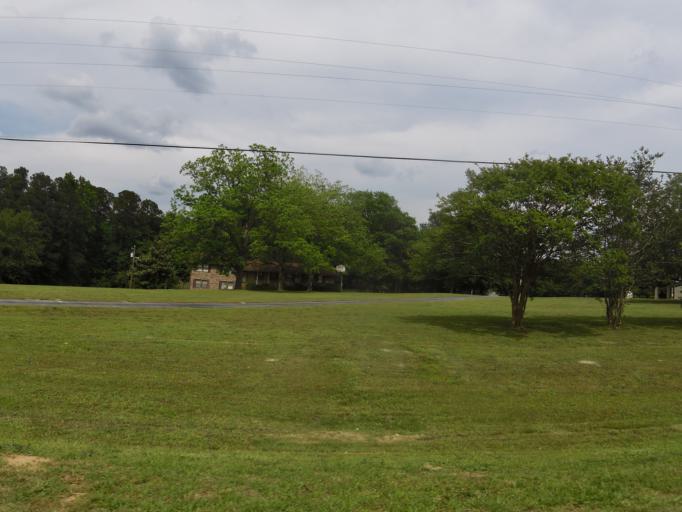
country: US
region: Georgia
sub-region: McDuffie County
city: Thomson
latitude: 33.4404
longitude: -82.4916
